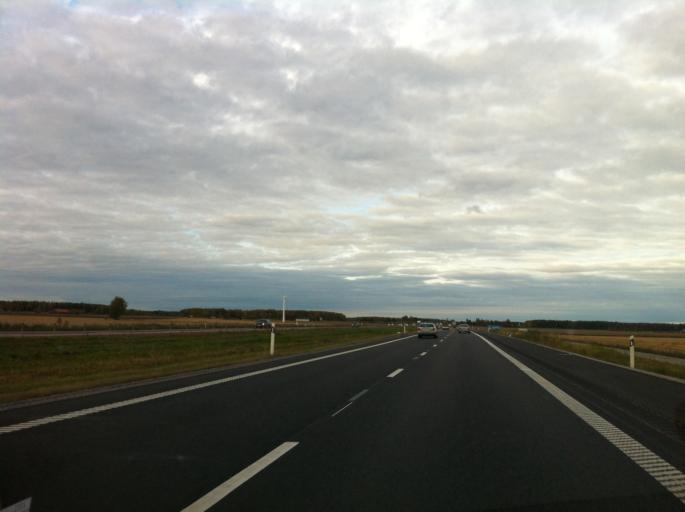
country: SE
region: OErebro
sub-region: Kumla Kommun
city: Kumla
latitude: 59.1670
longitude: 15.1119
